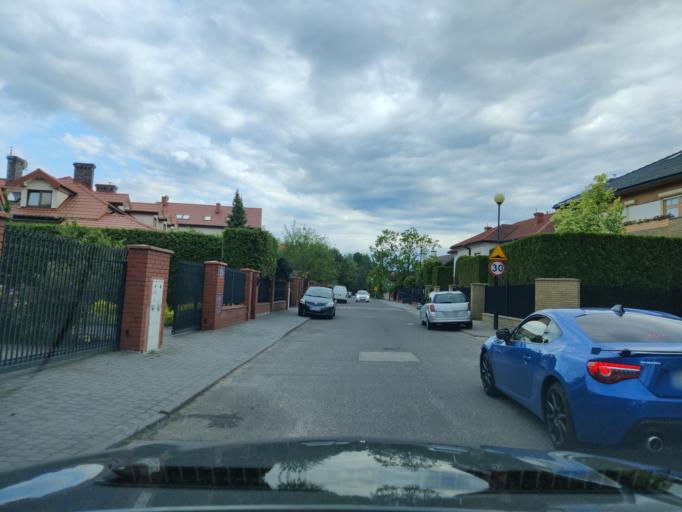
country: PL
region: Masovian Voivodeship
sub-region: Warszawa
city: Kabaty
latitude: 52.1303
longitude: 21.0932
